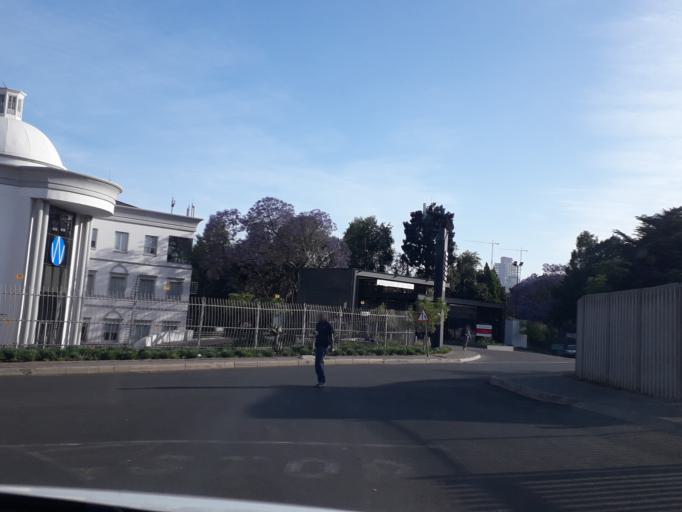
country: ZA
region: Gauteng
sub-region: City of Johannesburg Metropolitan Municipality
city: Johannesburg
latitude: -26.1161
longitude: 28.0464
